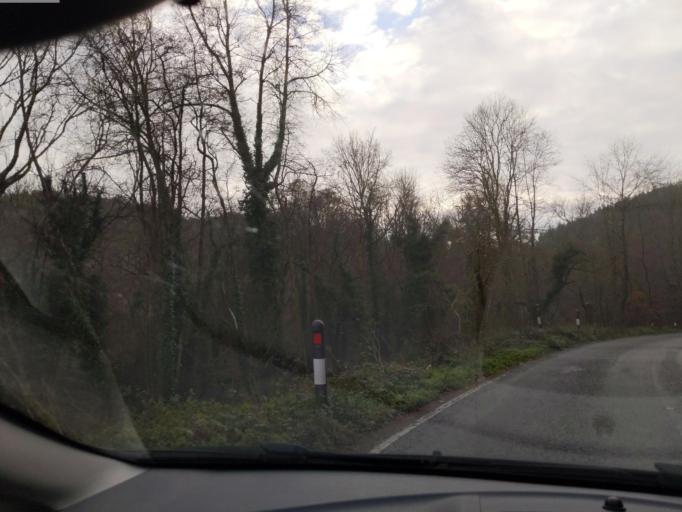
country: GB
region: England
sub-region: Cornwall
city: Looe
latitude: 50.3834
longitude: -4.3887
